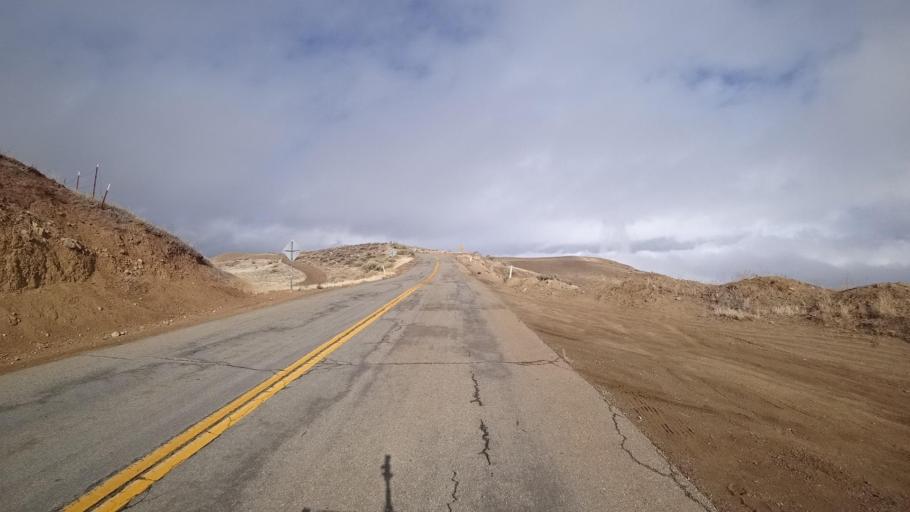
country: US
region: California
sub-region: Kern County
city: Maricopa
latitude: 34.8973
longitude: -119.3655
